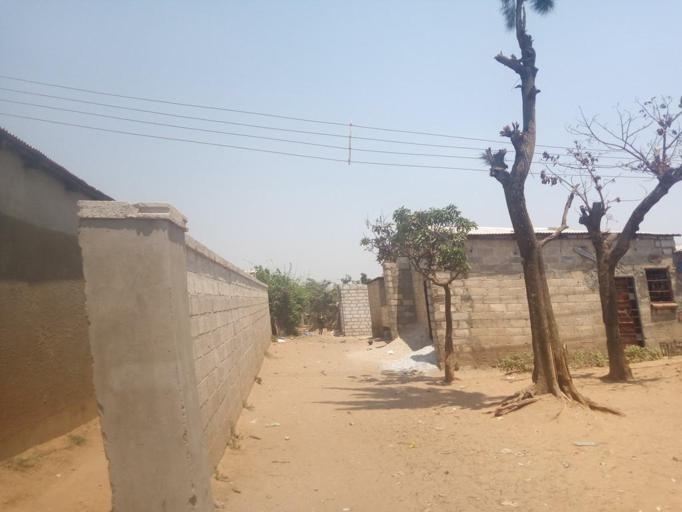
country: ZM
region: Lusaka
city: Lusaka
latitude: -15.4054
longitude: 28.3680
